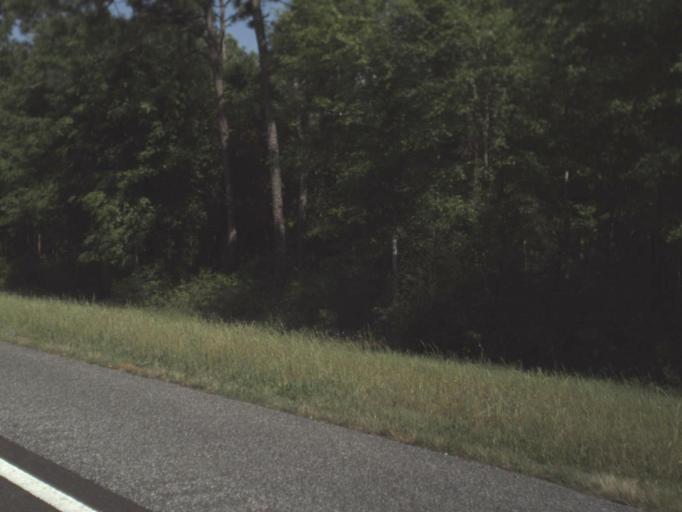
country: US
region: Florida
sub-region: Santa Rosa County
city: East Milton
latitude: 30.6411
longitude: -86.9086
